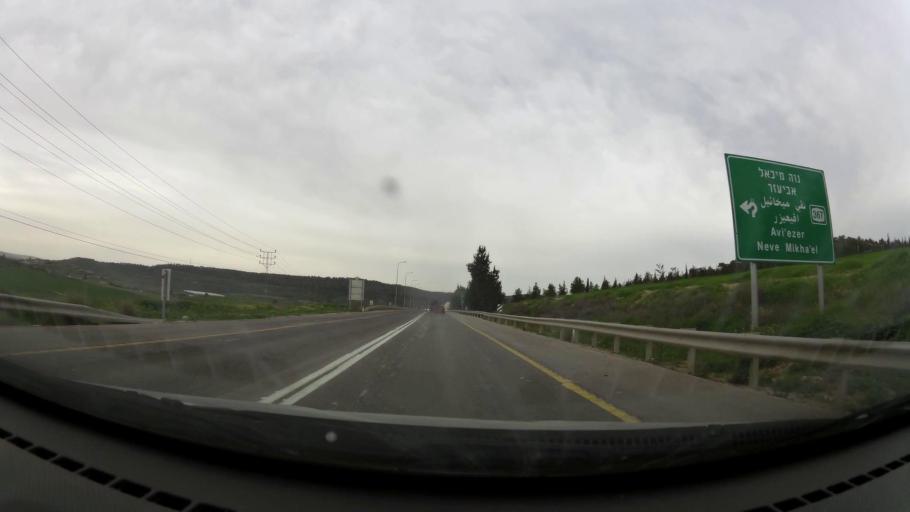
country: IL
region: Jerusalem
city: Bet Shemesh
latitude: 31.6857
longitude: 35.0013
